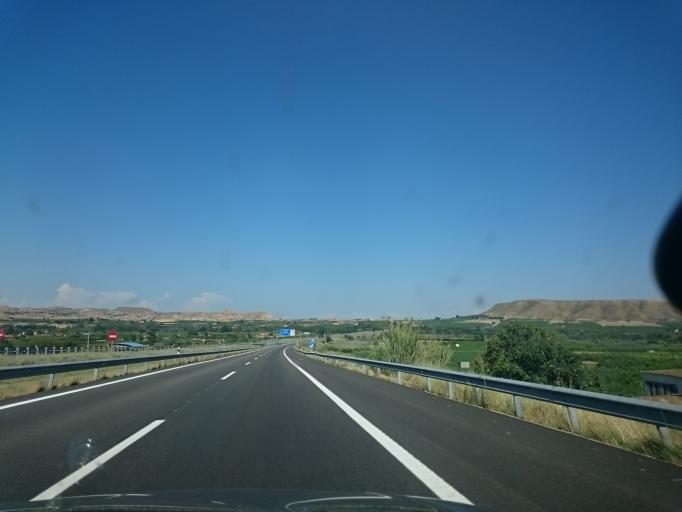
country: ES
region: Aragon
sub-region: Provincia de Huesca
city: Fraga
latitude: 41.4886
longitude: 0.3343
